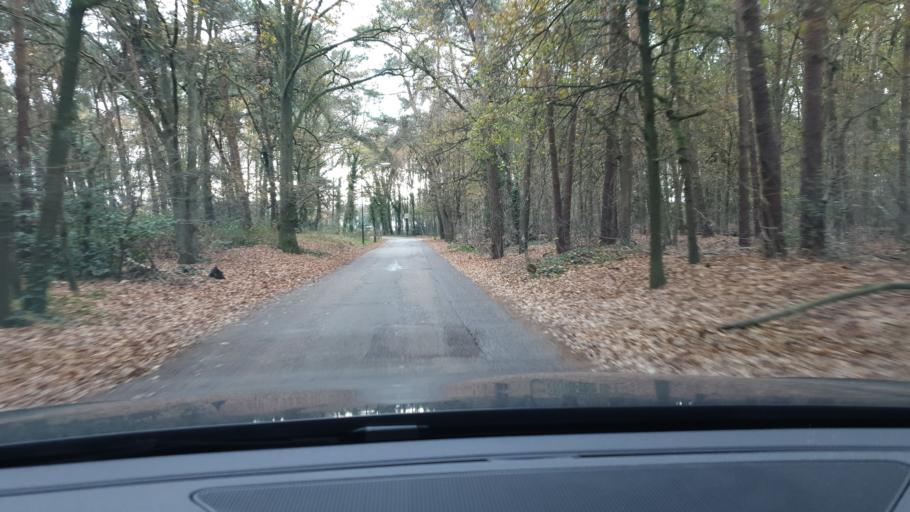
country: NL
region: North Brabant
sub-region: Gemeente Waalre
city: Waalre
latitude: 51.3818
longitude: 5.4436
